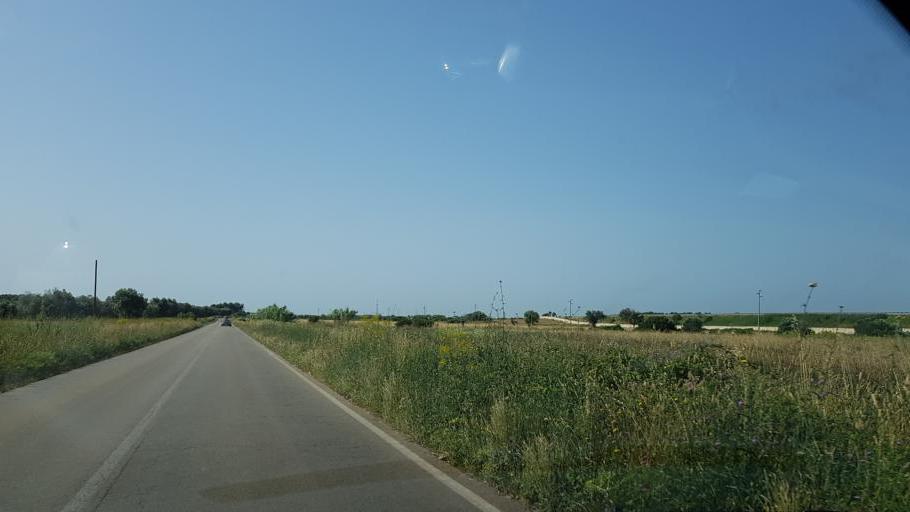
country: IT
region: Apulia
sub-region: Provincia di Lecce
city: Porto Cesareo
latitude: 40.3333
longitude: 17.8513
